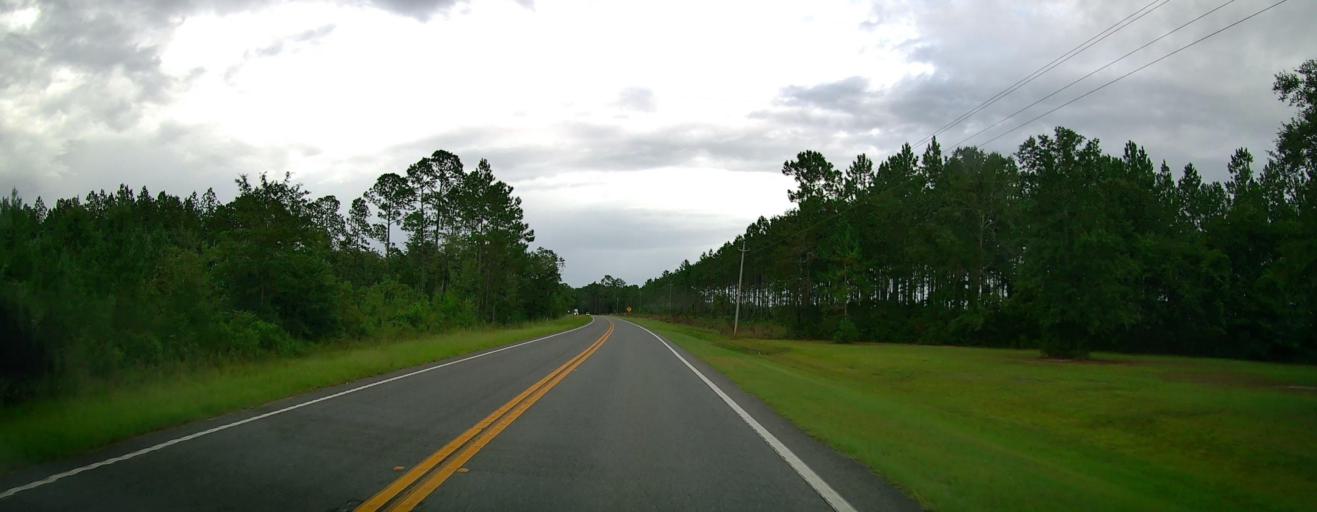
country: US
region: Georgia
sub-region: Ware County
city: Deenwood
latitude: 31.2878
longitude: -82.5503
